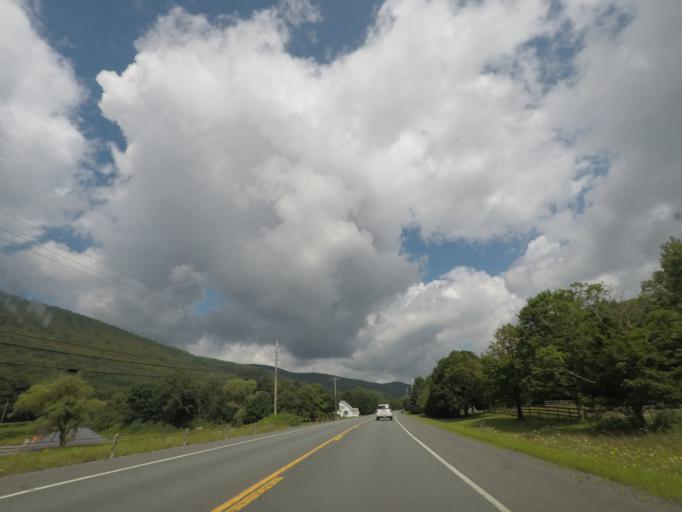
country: US
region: Massachusetts
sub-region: Berkshire County
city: Williamstown
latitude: 42.6502
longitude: -73.3643
